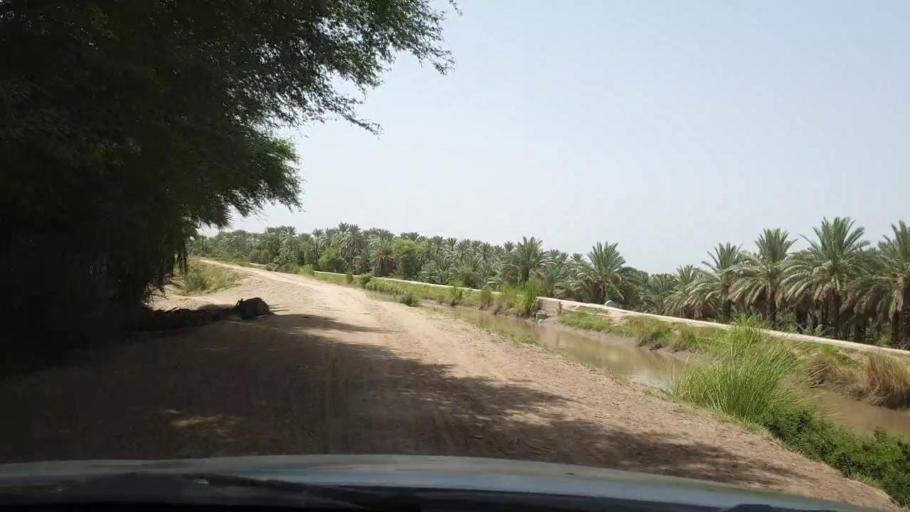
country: PK
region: Sindh
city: Pano Aqil
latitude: 27.8894
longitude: 69.1331
